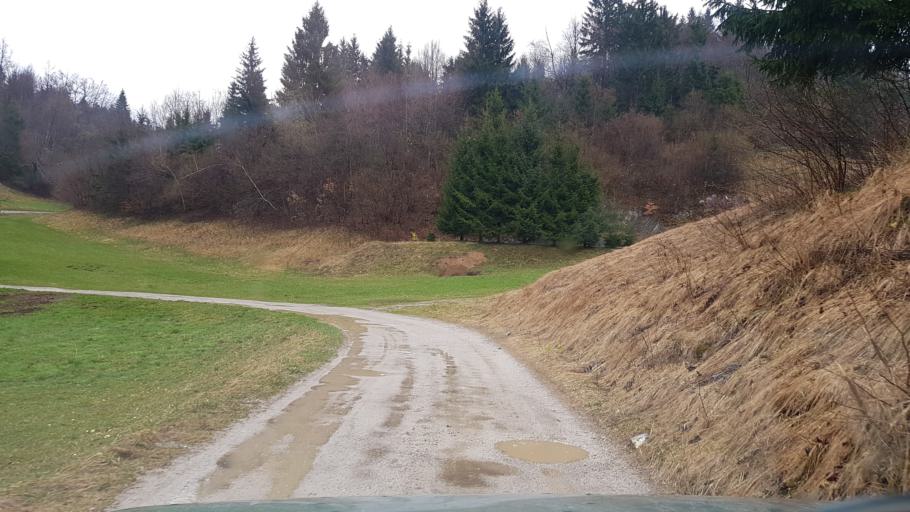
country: SI
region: Tolmin
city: Tolmin
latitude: 46.1357
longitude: 13.8492
